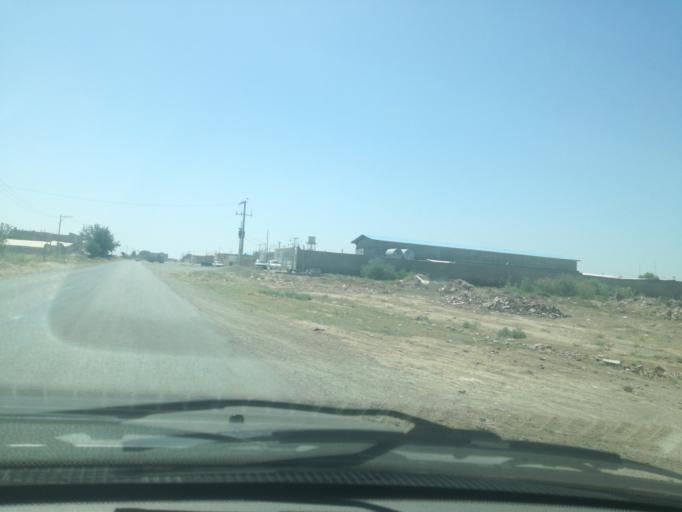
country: IR
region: Razavi Khorasan
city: Sarakhs
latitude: 36.5644
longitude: 61.1442
